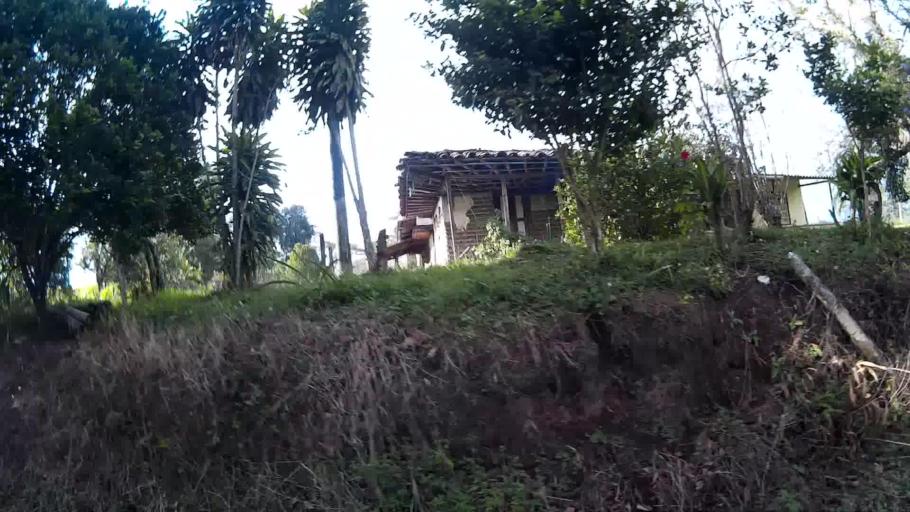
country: CO
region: Quindio
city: Filandia
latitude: 4.7063
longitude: -75.6908
